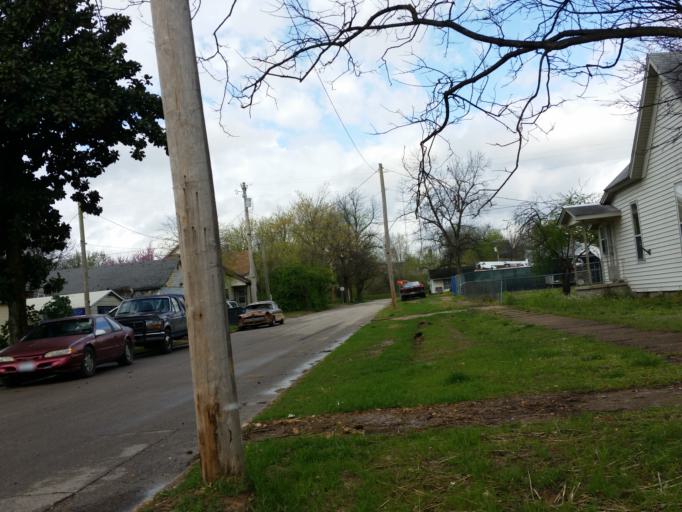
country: US
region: Missouri
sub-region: Butler County
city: Poplar Bluff
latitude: 36.7572
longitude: -90.3872
